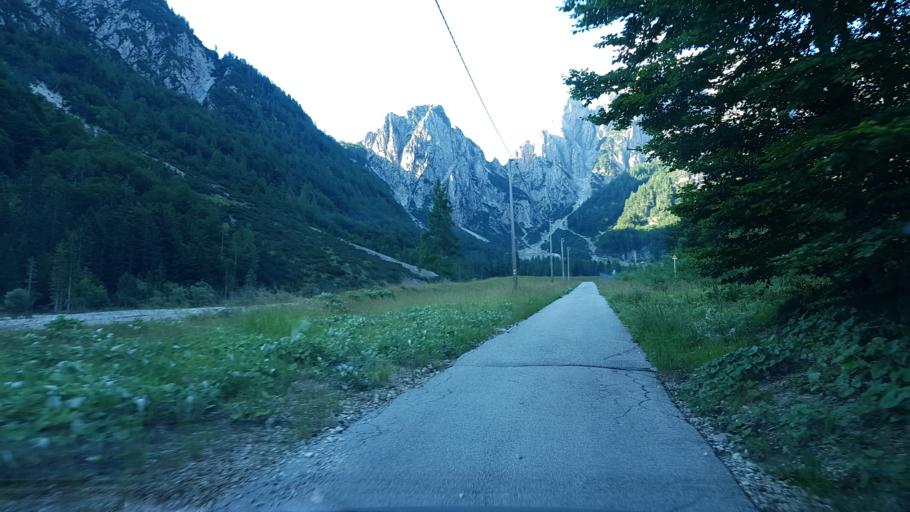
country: IT
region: Friuli Venezia Giulia
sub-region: Provincia di Udine
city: Pontebba
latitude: 46.4918
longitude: 13.2551
